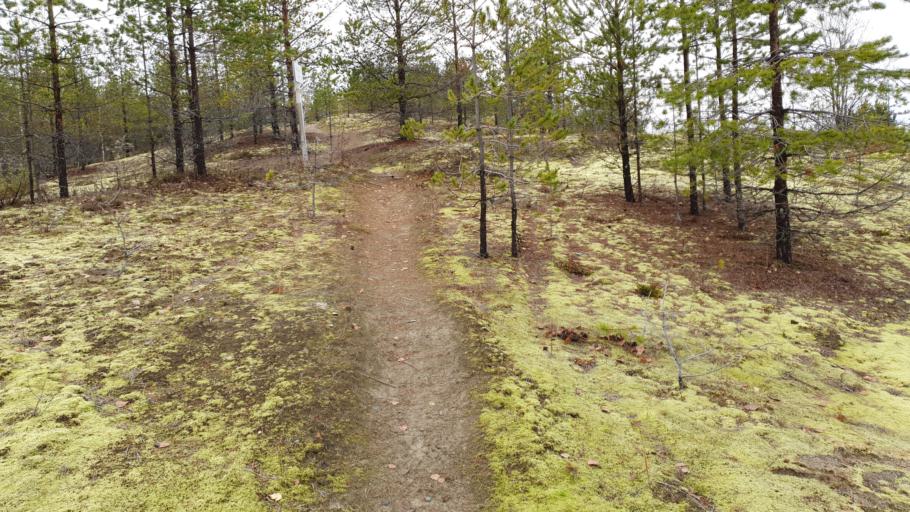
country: FI
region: Kainuu
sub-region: Kehys-Kainuu
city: Kuhmo
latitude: 64.1520
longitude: 29.3940
